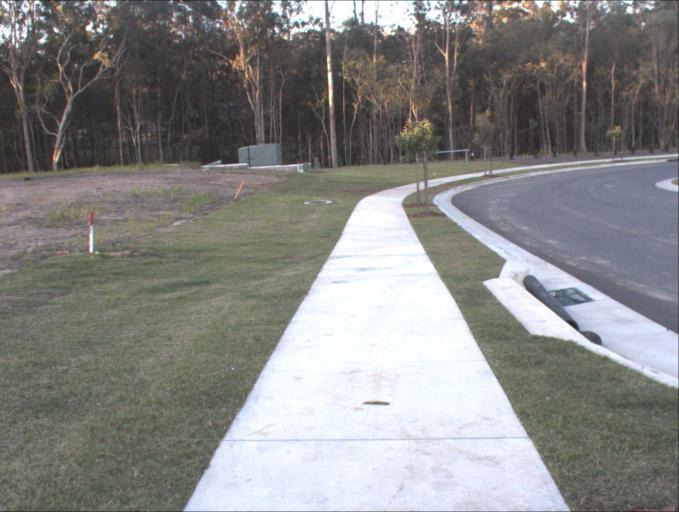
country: AU
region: Queensland
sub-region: Logan
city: North Maclean
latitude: -27.7980
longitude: 152.9531
